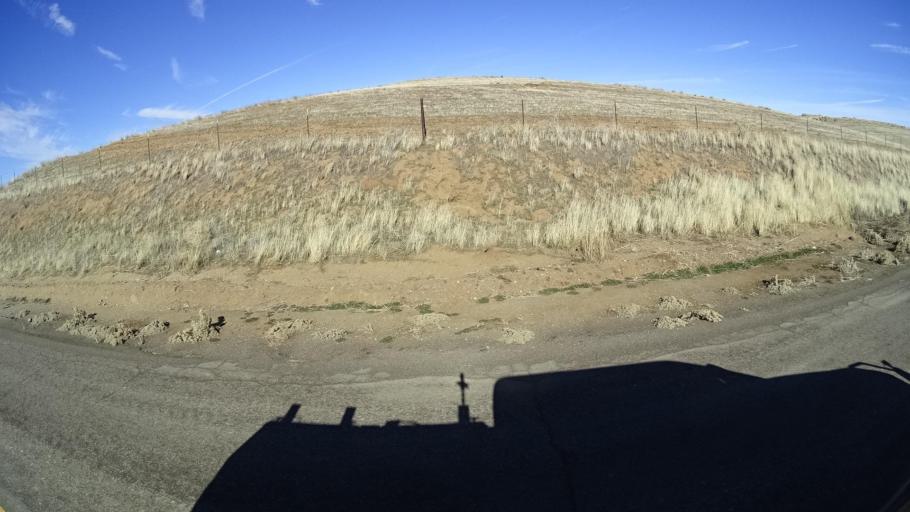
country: US
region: California
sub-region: Kern County
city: Maricopa
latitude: 34.9074
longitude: -119.3916
